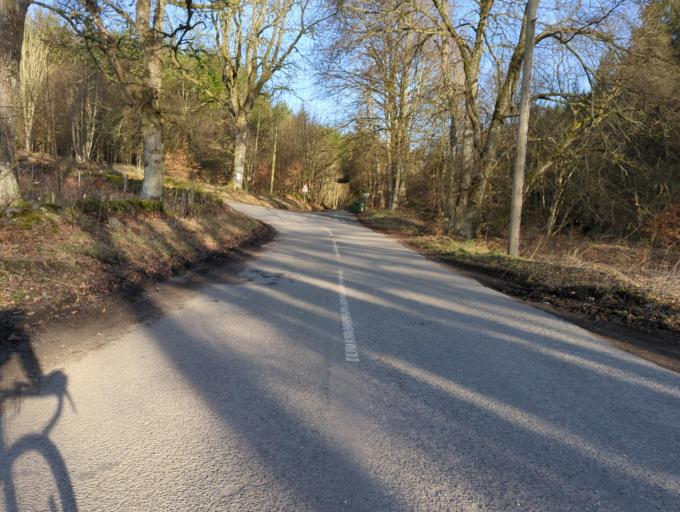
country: GB
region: Scotland
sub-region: Perth and Kinross
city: Methven
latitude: 56.4587
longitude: -3.5883
